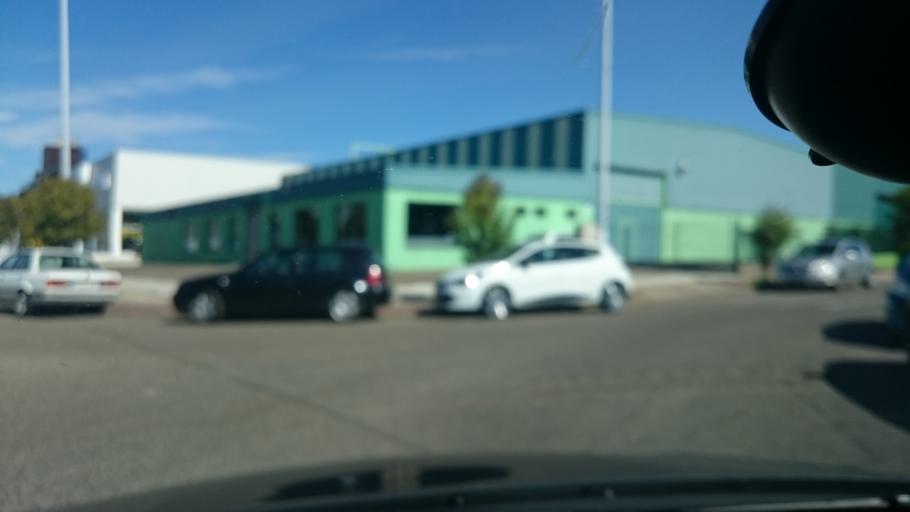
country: ES
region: Castille and Leon
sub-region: Provincia de Leon
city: Ponferrada
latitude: 42.5537
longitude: -6.6151
